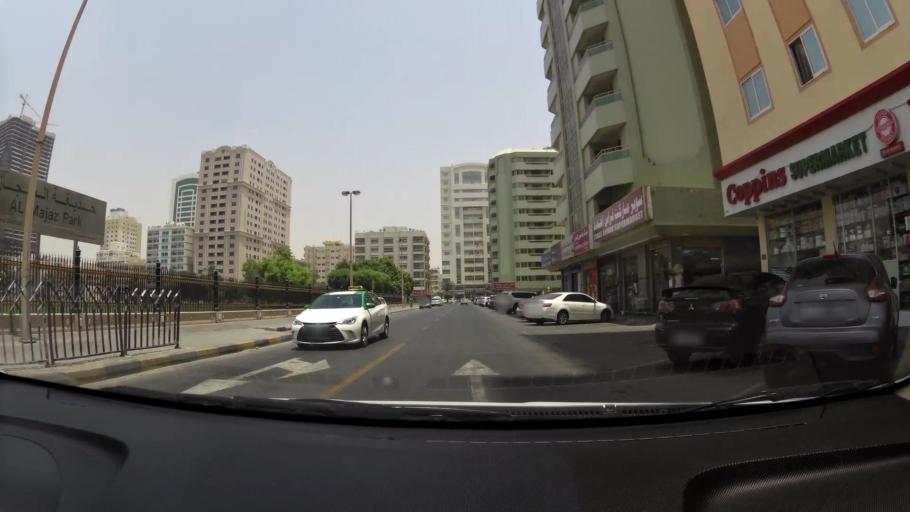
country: AE
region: Ash Shariqah
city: Sharjah
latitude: 25.3234
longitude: 55.3864
